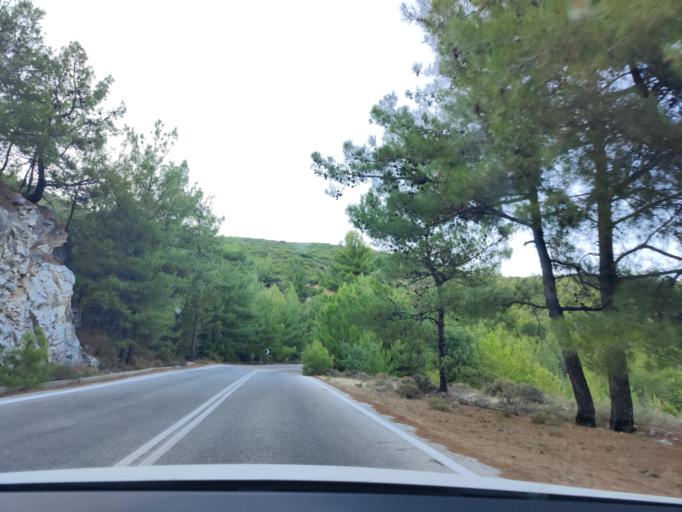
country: GR
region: East Macedonia and Thrace
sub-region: Nomos Kavalas
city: Potamia
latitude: 40.6240
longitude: 24.7619
